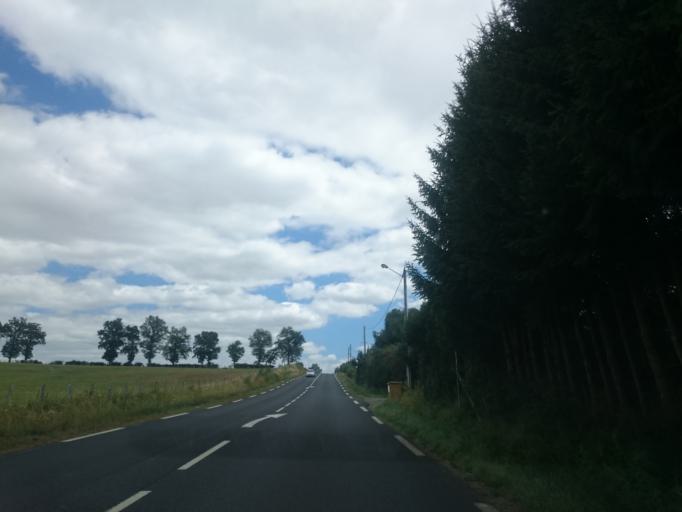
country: FR
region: Auvergne
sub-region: Departement du Cantal
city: Saint-Paul-des-Landes
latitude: 44.9530
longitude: 2.2864
